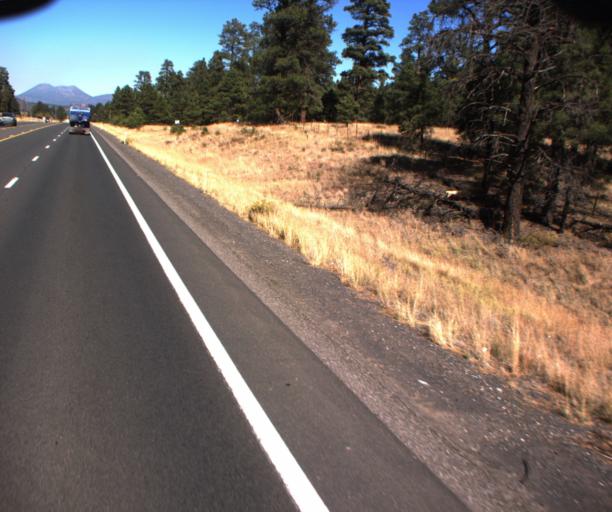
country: US
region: Arizona
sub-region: Coconino County
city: Flagstaff
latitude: 35.2790
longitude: -111.5427
